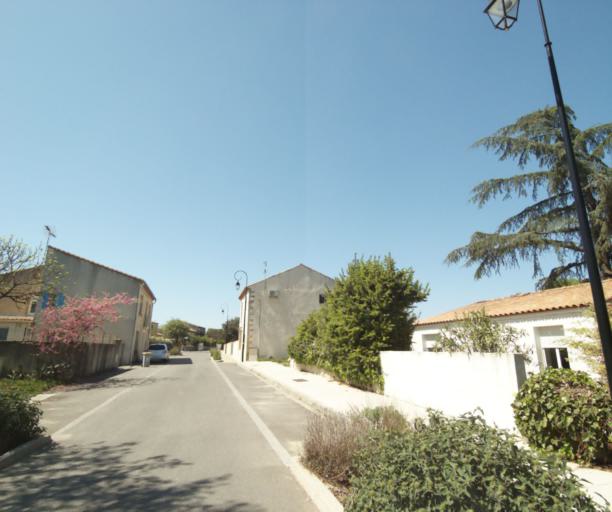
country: FR
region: Languedoc-Roussillon
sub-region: Departement de l'Herault
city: Beaulieu
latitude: 43.7271
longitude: 4.0262
